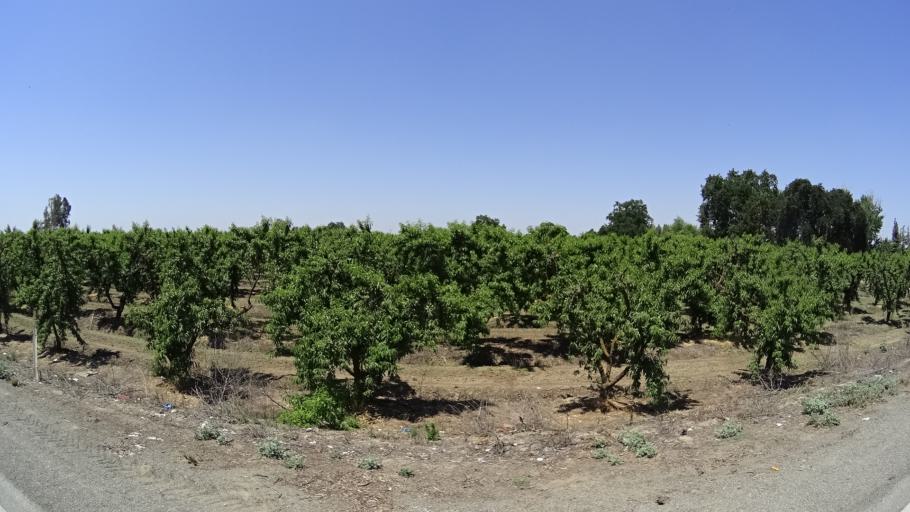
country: US
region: California
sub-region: Fresno County
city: Laton
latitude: 36.4248
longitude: -119.6863
